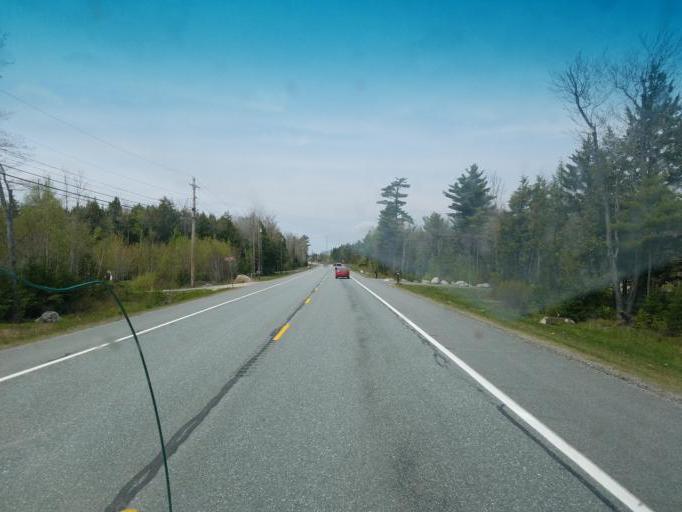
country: US
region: Maine
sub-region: Hancock County
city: Surry
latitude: 44.6090
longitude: -68.5196
